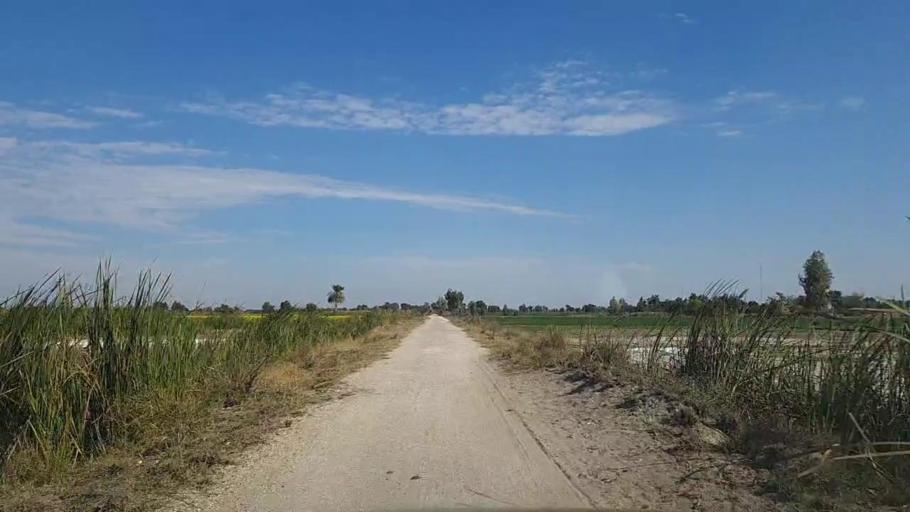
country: PK
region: Sindh
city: Khadro
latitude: 26.2733
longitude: 68.8110
